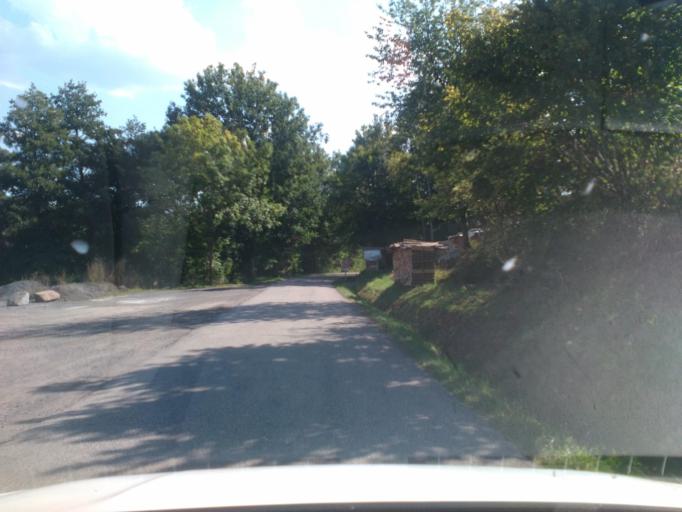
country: FR
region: Lorraine
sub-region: Departement des Vosges
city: Ban-de-Laveline
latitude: 48.3135
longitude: 7.0818
